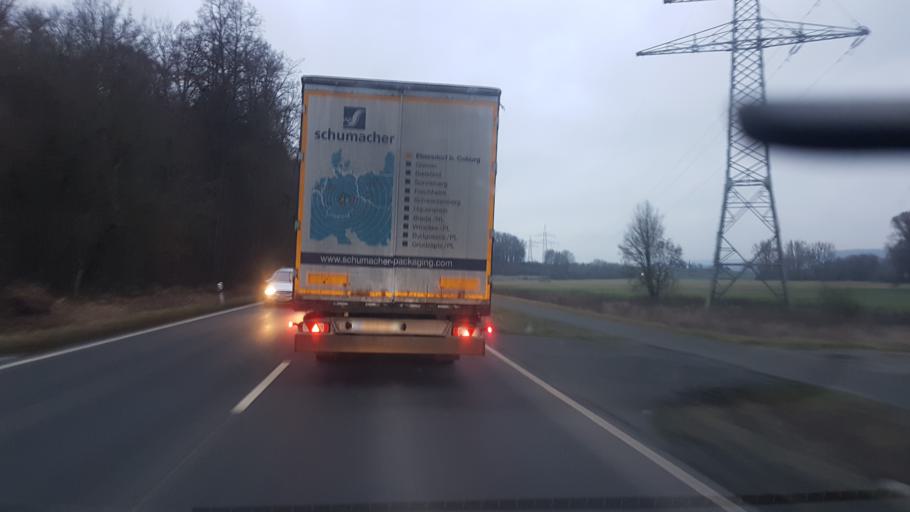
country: DE
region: Bavaria
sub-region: Regierungsbezirk Unterfranken
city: Rentweinsdorf
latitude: 50.0706
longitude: 10.7953
